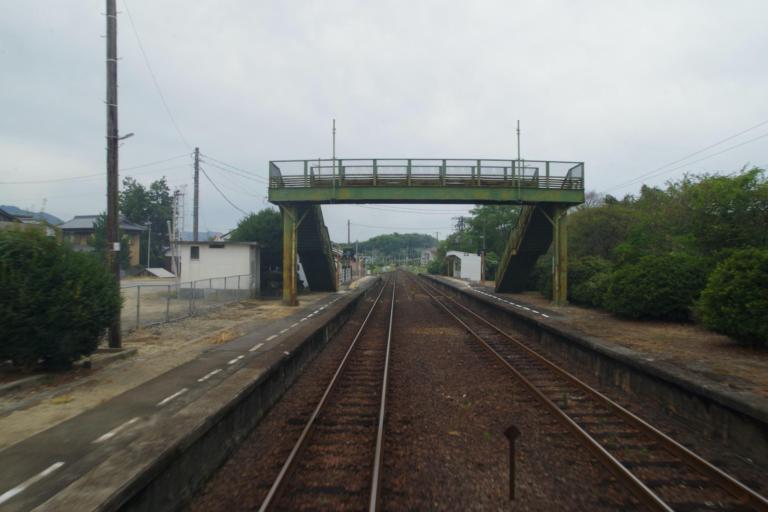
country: JP
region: Tokushima
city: Ikedacho
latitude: 34.1564
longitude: 133.8504
